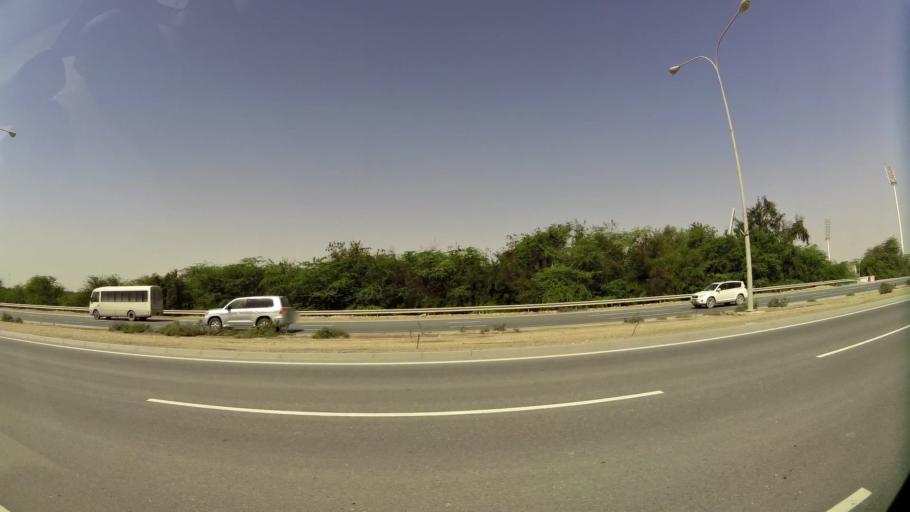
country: QA
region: Baladiyat ad Dawhah
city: Doha
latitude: 25.3728
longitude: 51.4973
